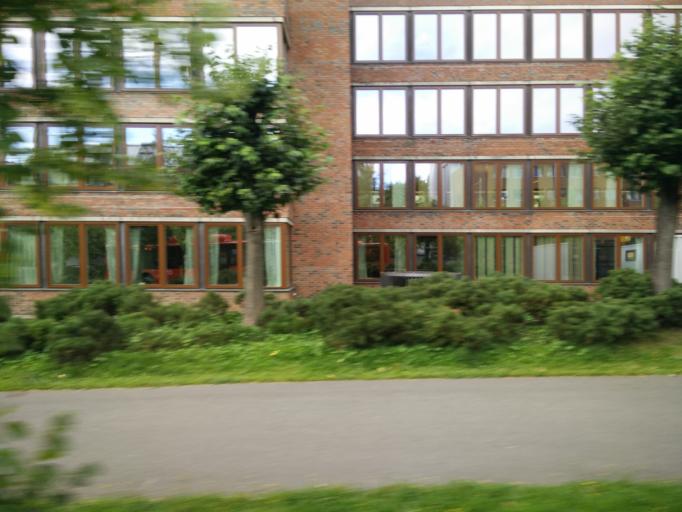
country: NO
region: Oslo
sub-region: Oslo
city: Sjolyststranda
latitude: 59.9318
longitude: 10.7068
